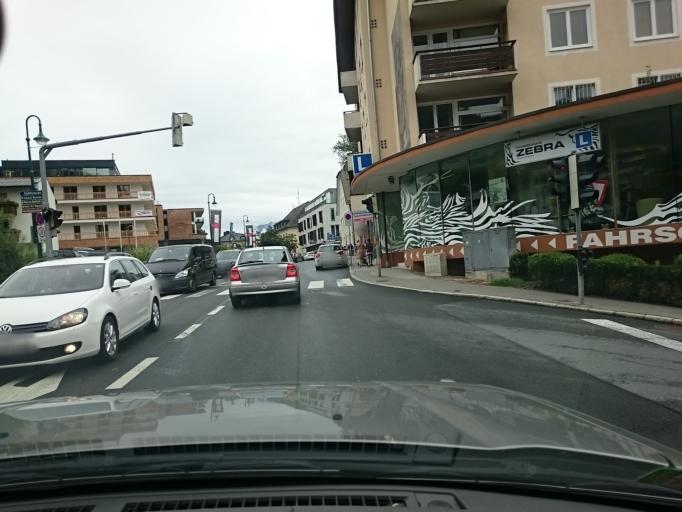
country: AT
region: Salzburg
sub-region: Politischer Bezirk Zell am See
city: Zell am See
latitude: 47.3208
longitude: 12.7956
